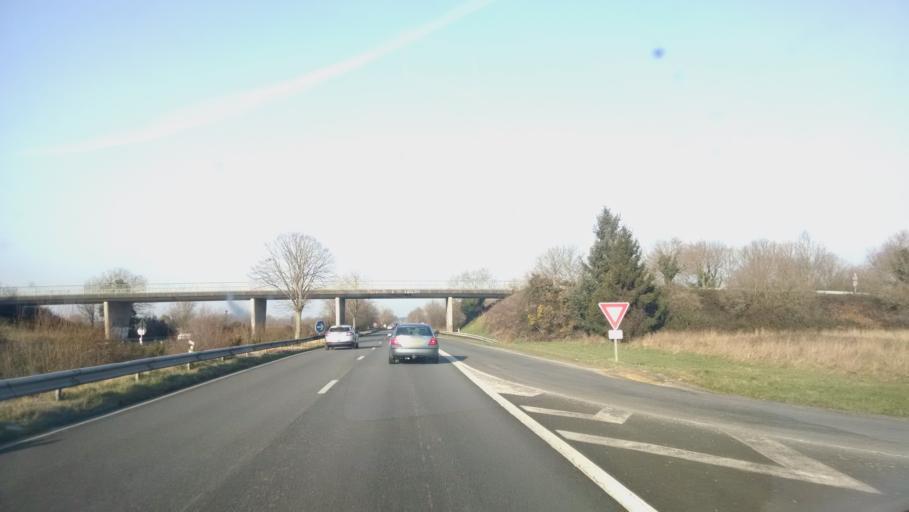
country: FR
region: Pays de la Loire
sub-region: Departement de la Loire-Atlantique
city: Malville
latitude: 47.3471
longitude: -1.8655
